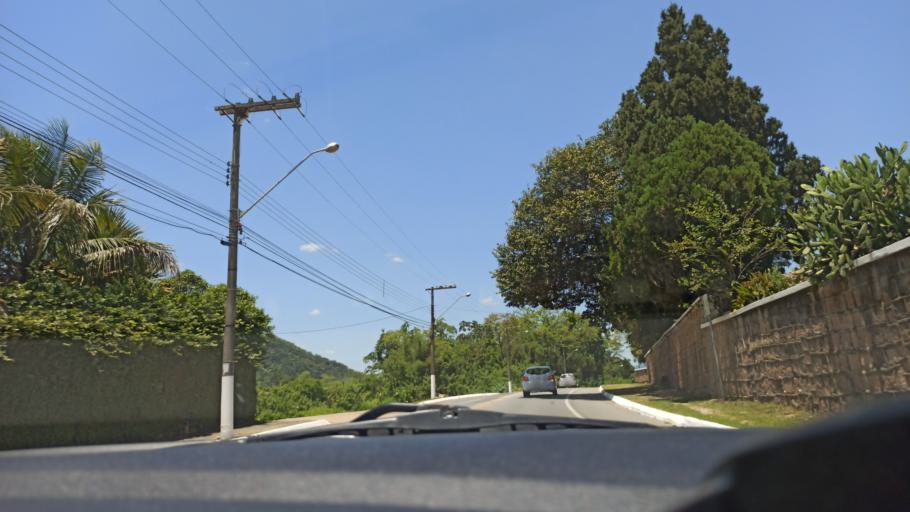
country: BR
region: Santa Catarina
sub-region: Indaial
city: Indaial
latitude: -26.8875
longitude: -49.2395
